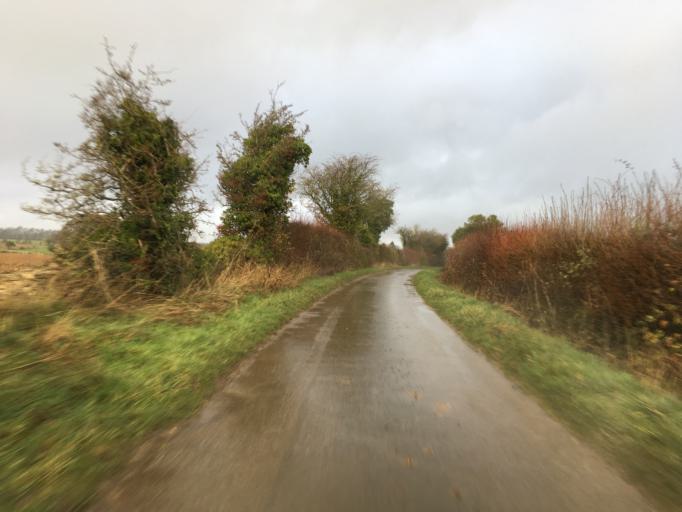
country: GB
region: England
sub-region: Wiltshire
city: Hankerton
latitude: 51.6532
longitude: -2.0676
